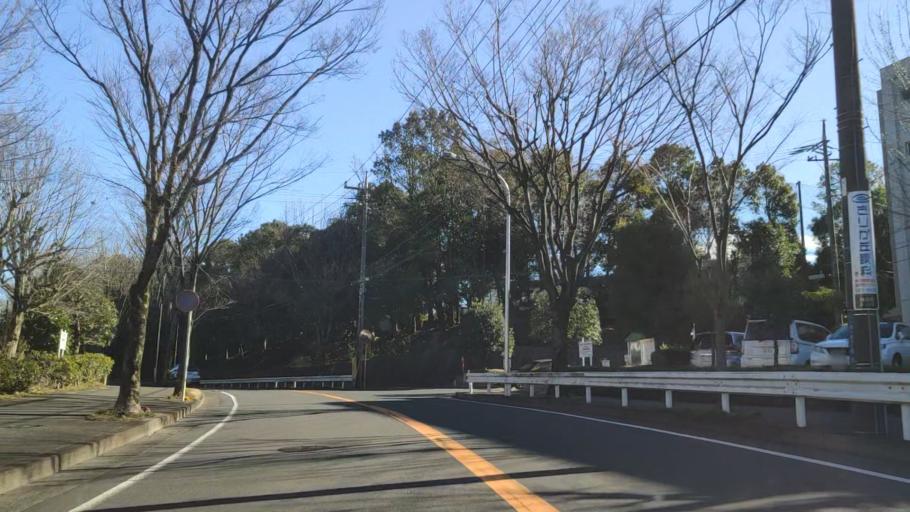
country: JP
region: Tokyo
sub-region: Machida-shi
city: Machida
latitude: 35.5116
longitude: 139.5013
